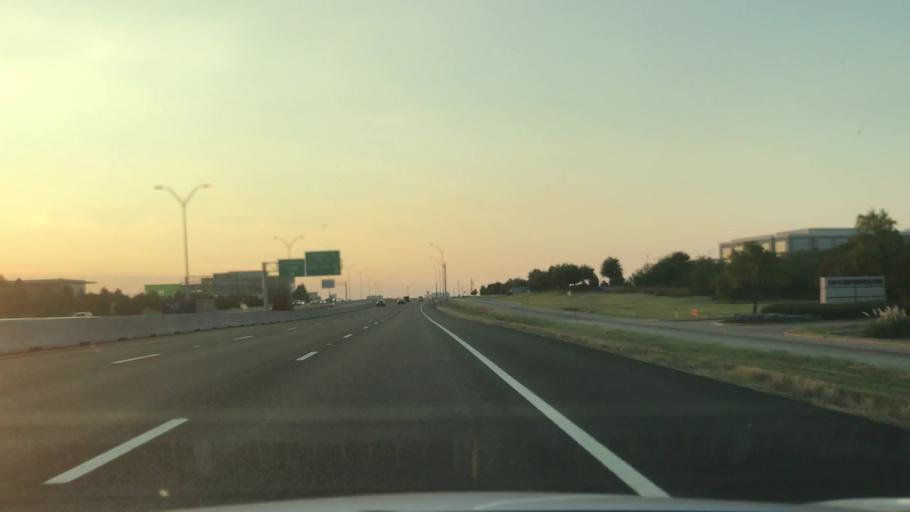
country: US
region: Texas
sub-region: Dallas County
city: Coppell
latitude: 32.8973
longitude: -96.9750
